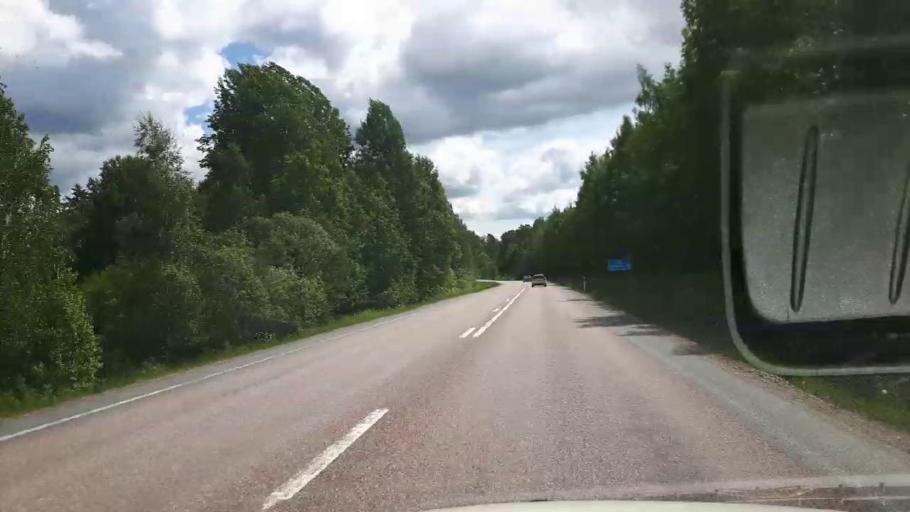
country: SE
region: Dalarna
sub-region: Saters Kommun
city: Saeter
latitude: 60.4775
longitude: 15.7811
